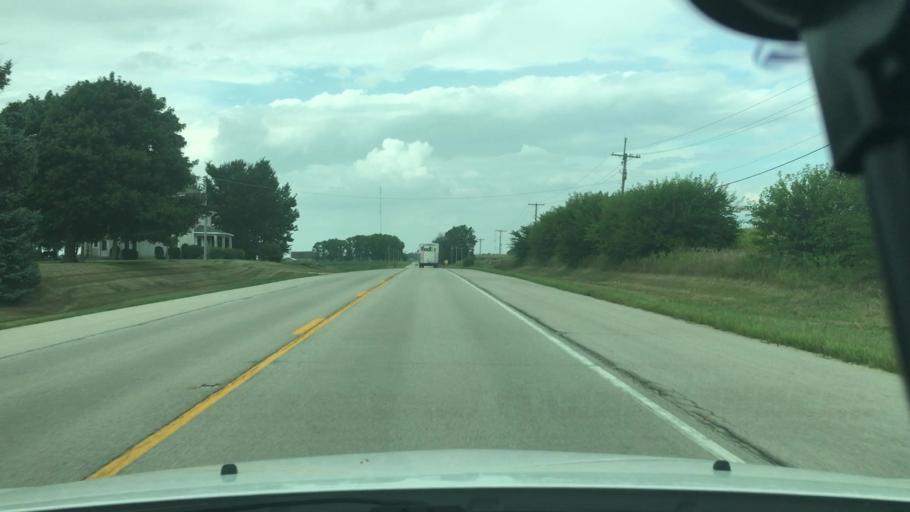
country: US
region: Illinois
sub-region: DeKalb County
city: DeKalb
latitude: 41.8590
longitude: -88.7538
